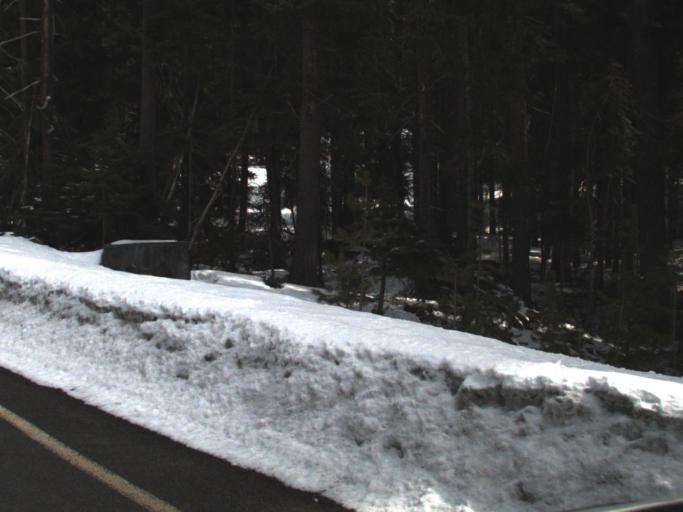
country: US
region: Washington
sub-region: Kittitas County
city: Cle Elum
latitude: 46.9330
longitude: -121.3575
